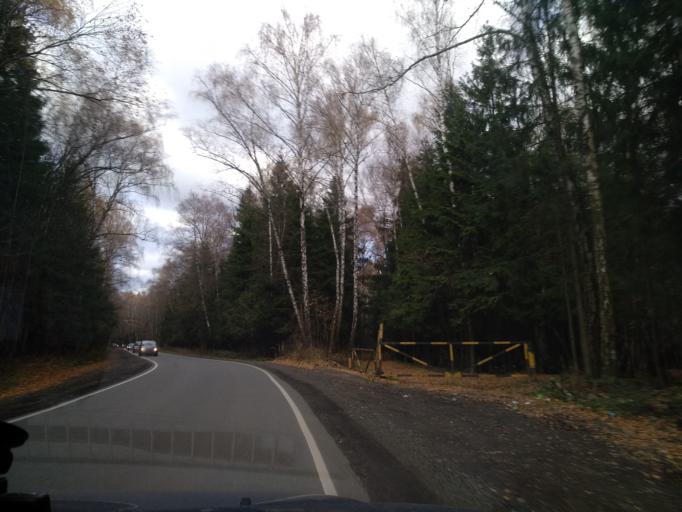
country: RU
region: Moscow
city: Lianozovo
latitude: 55.9120
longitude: 37.6105
